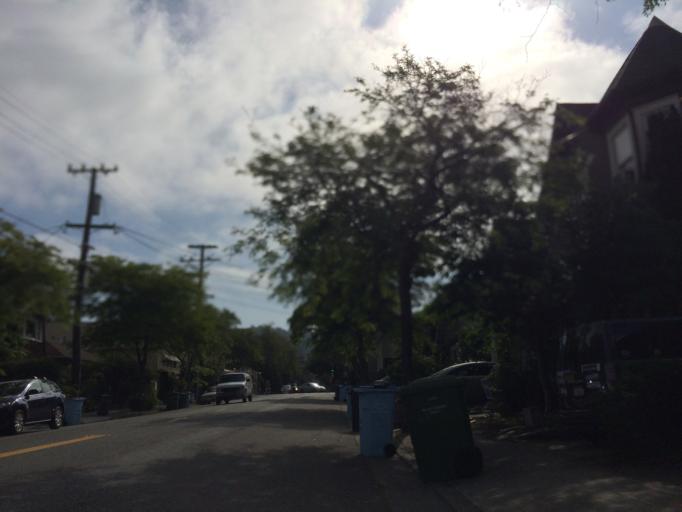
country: US
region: California
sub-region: Alameda County
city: Berkeley
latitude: 37.8777
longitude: -122.2747
